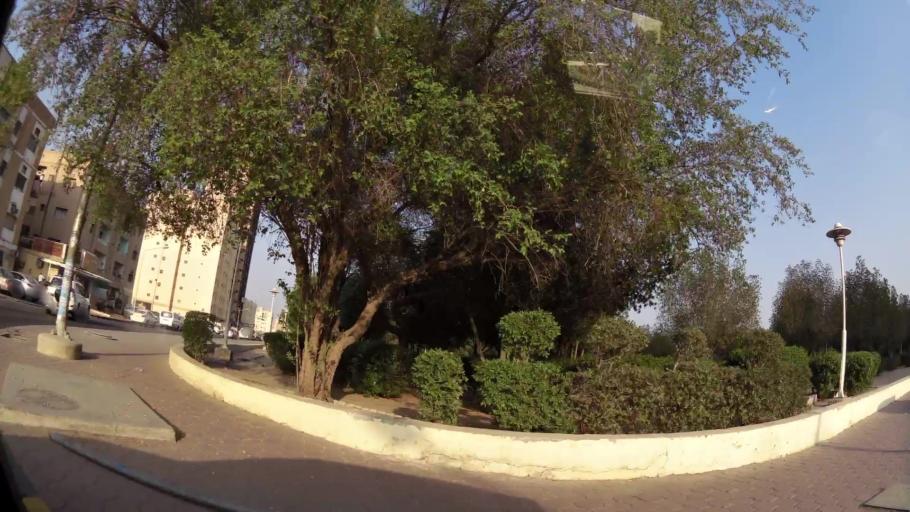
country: KW
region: Muhafazat Hawalli
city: As Salimiyah
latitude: 29.3256
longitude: 48.0644
